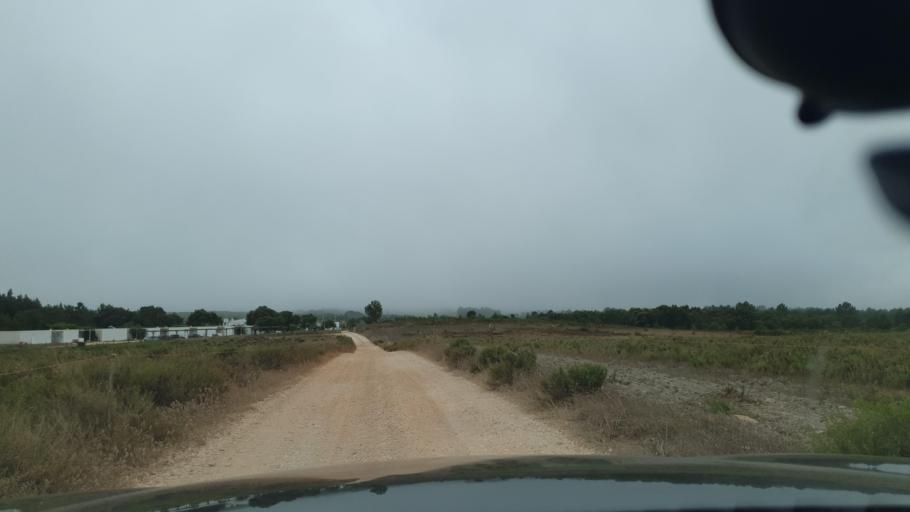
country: PT
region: Beja
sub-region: Odemira
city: Sao Teotonio
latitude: 37.4953
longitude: -8.6846
